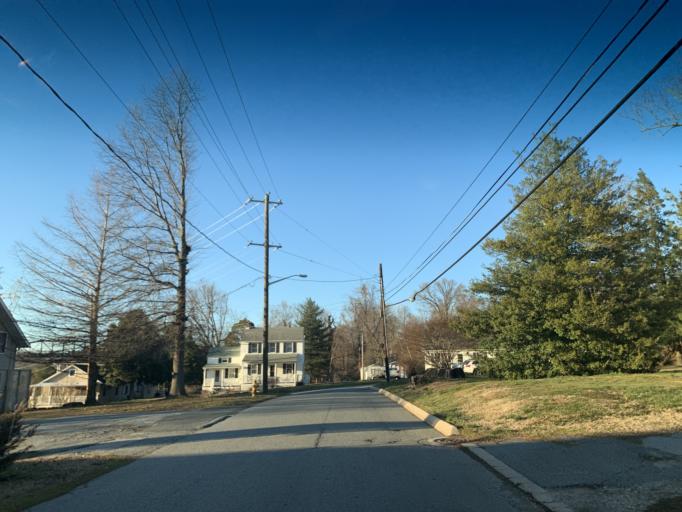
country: US
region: Maryland
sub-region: Cecil County
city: Perryville
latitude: 39.5670
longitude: -76.0775
